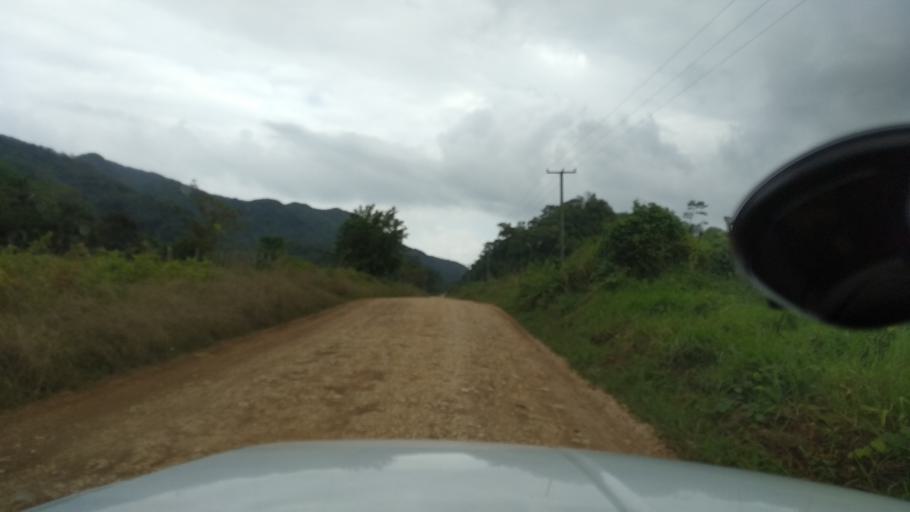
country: BZ
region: Toledo
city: Punta Gorda
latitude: 16.2043
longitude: -89.0320
